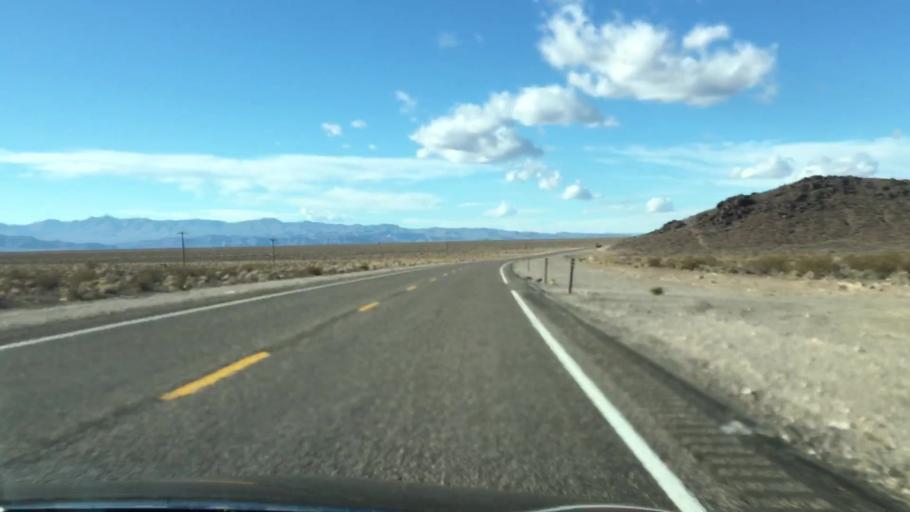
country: US
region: Nevada
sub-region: Nye County
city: Beatty
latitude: 37.1789
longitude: -116.9297
